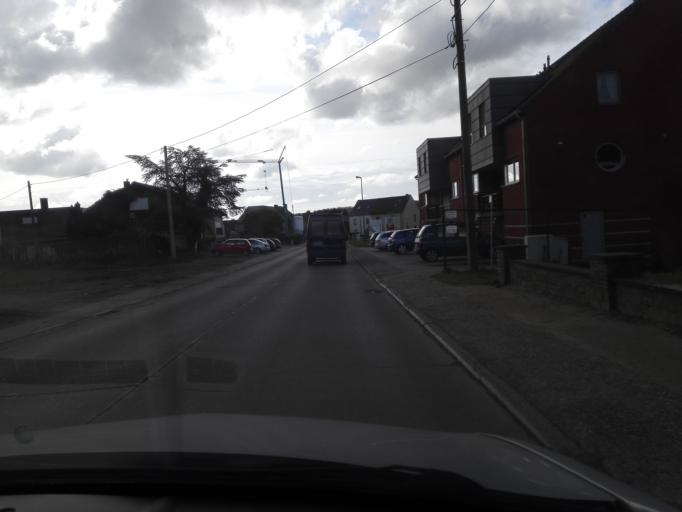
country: BE
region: Flanders
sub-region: Provincie Vlaams-Brabant
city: Bekkevoort
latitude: 50.9389
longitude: 4.9060
